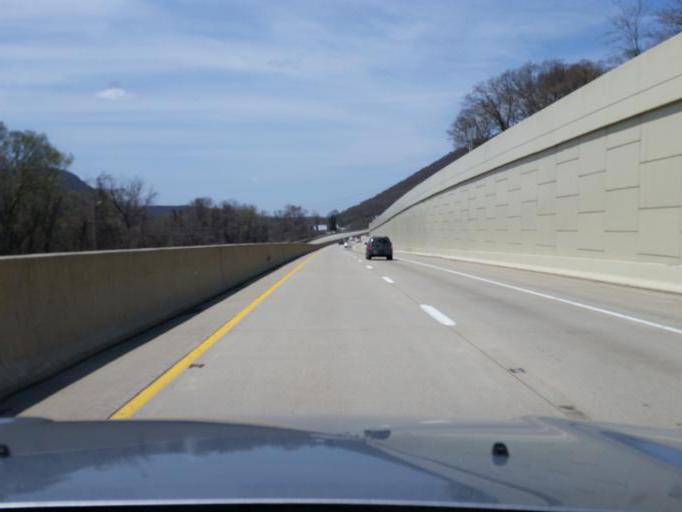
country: US
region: Pennsylvania
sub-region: Perry County
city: Duncannon
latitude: 40.3740
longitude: -76.9973
